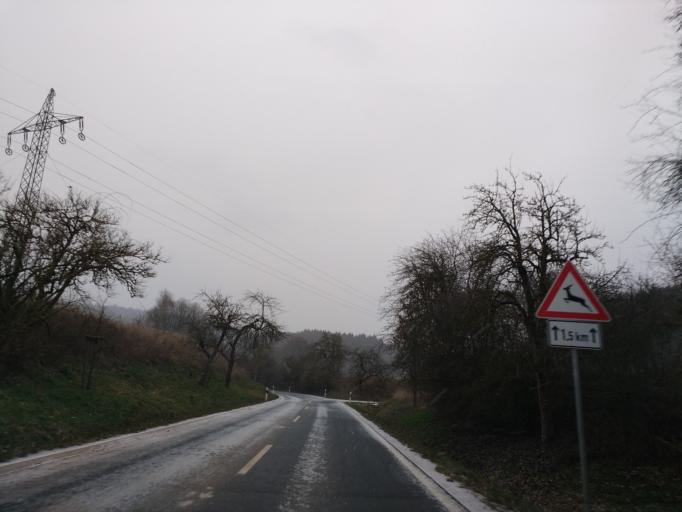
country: DE
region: Hesse
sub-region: Regierungsbezirk Kassel
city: Cornberg
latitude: 51.0719
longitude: 9.7805
